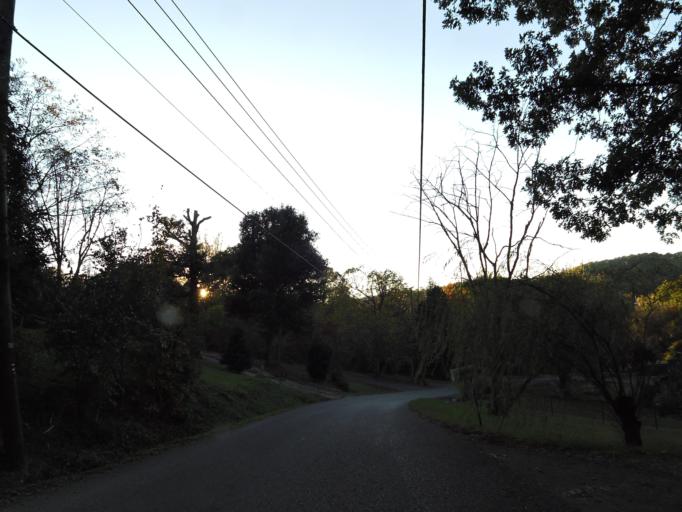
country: US
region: Tennessee
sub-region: Knox County
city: Knoxville
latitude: 36.0138
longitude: -84.0029
